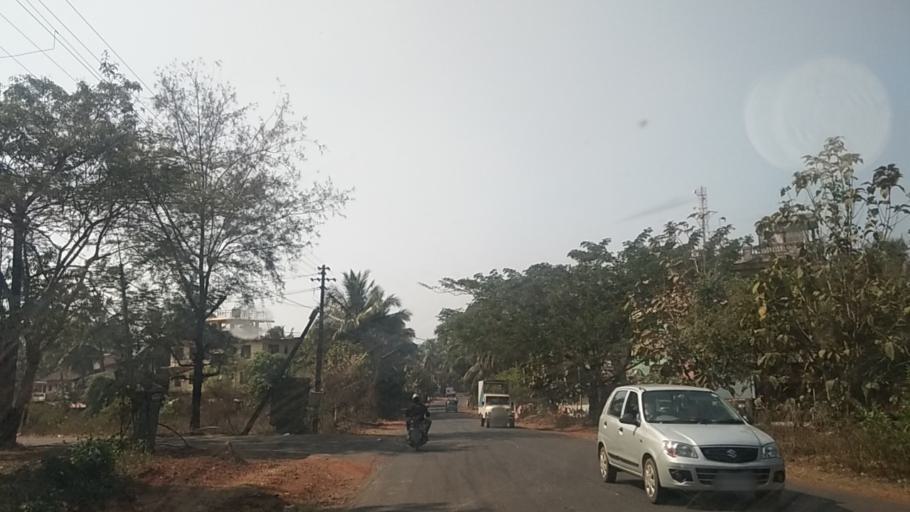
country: IN
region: Goa
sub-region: North Goa
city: Dicholi
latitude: 15.5854
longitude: 73.9579
